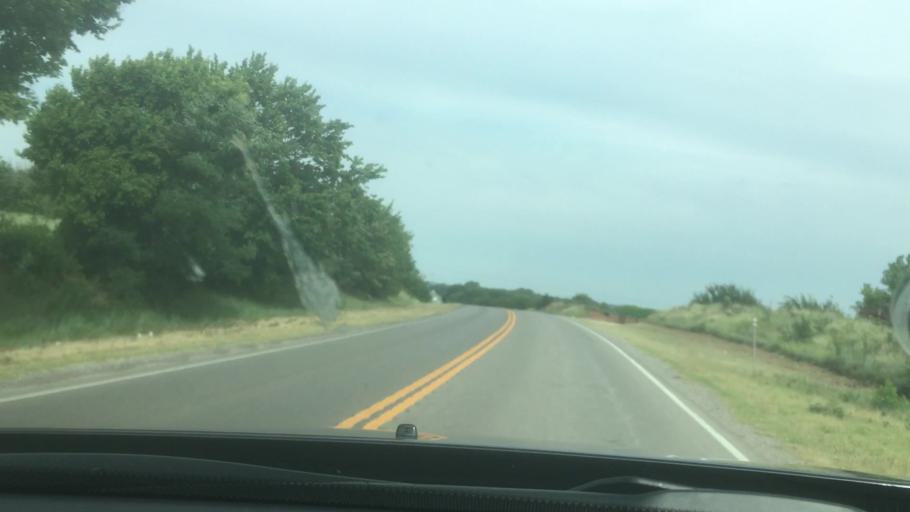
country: US
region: Oklahoma
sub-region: Garvin County
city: Maysville
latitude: 34.8121
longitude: -97.3803
